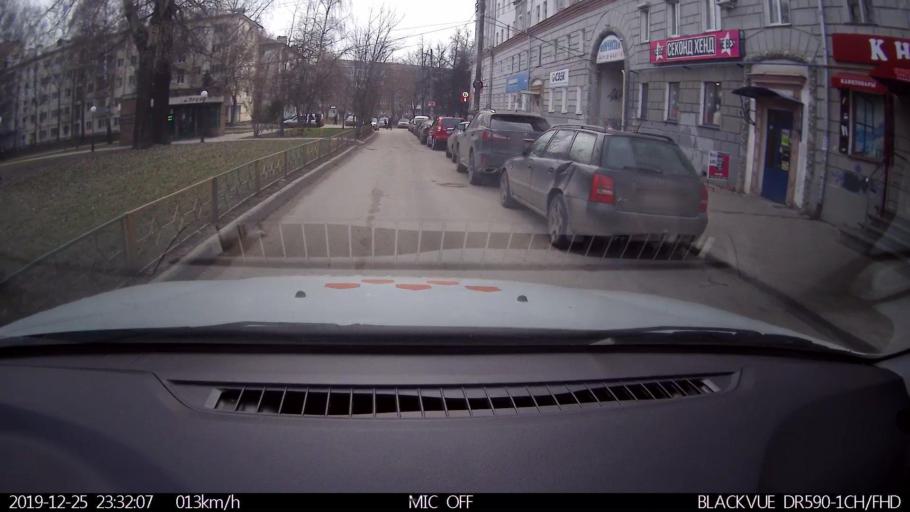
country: RU
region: Nizjnij Novgorod
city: Neklyudovo
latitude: 56.3490
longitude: 43.8658
